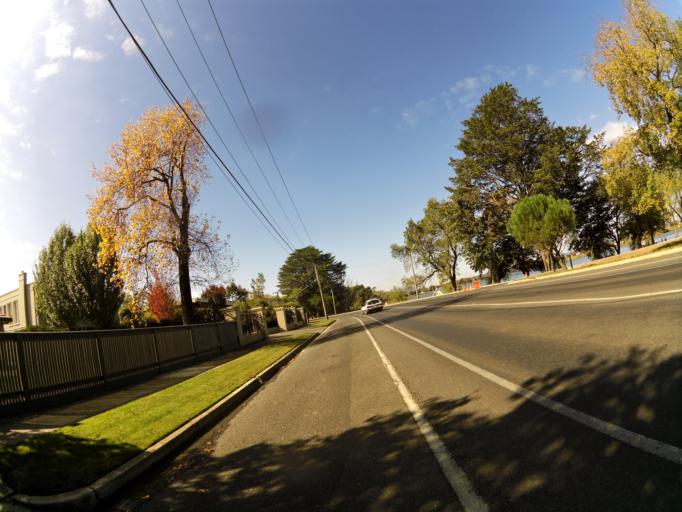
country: AU
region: Victoria
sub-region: Ballarat North
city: Lake Wendouree
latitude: -37.5438
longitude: 143.8351
